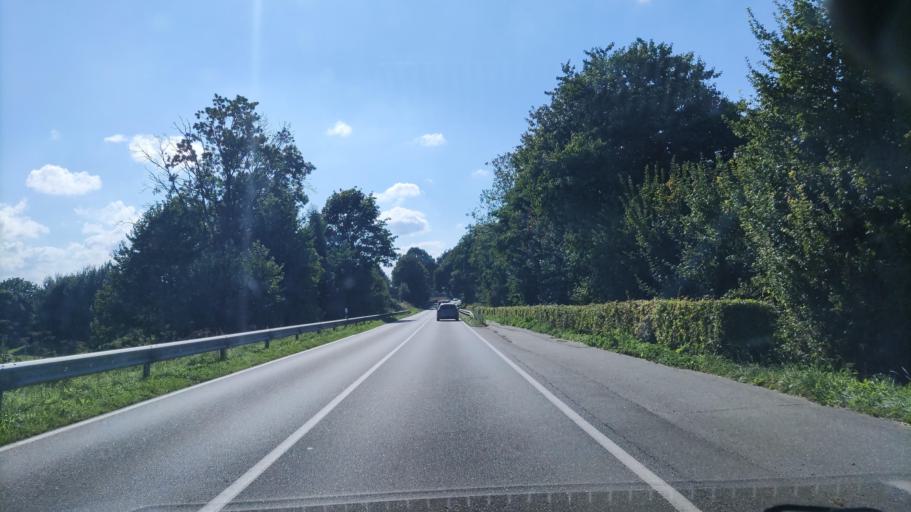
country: DE
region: Schleswig-Holstein
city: Osterby
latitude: 54.4516
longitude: 9.7578
